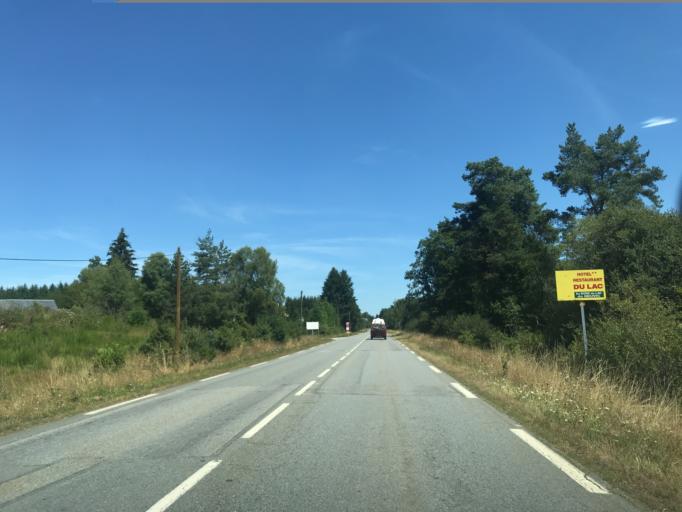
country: FR
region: Limousin
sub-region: Departement de la Correze
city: Meymac
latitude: 45.4968
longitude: 2.2202
